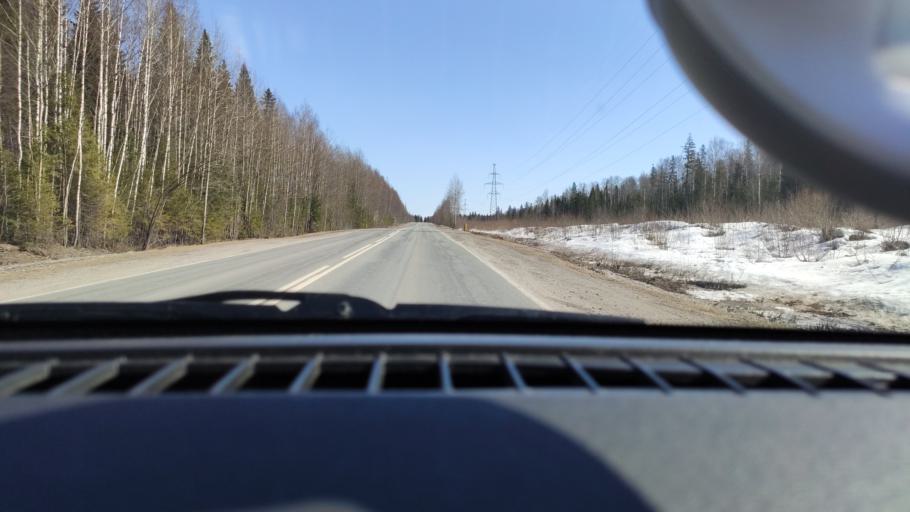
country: RU
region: Perm
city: Perm
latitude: 58.1375
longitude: 56.2810
